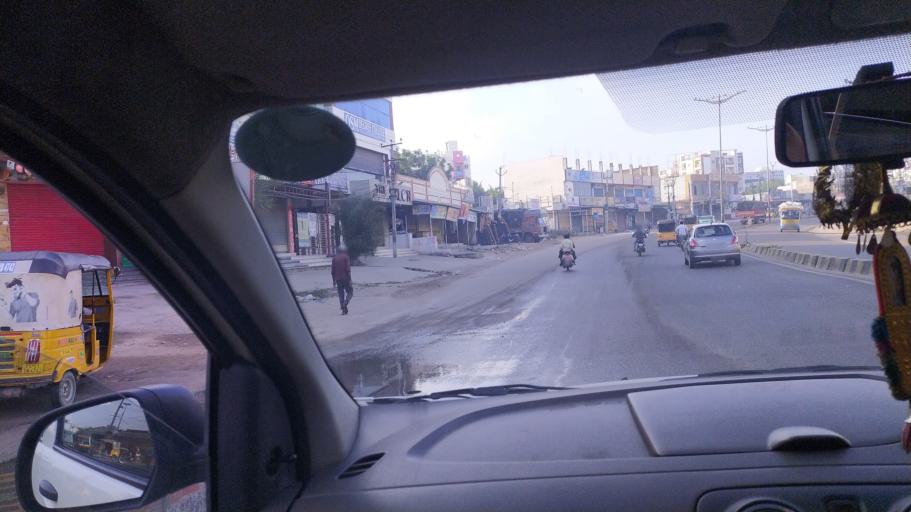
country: IN
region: Telangana
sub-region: Rangareddi
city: Balapur
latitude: 17.3165
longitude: 78.4663
